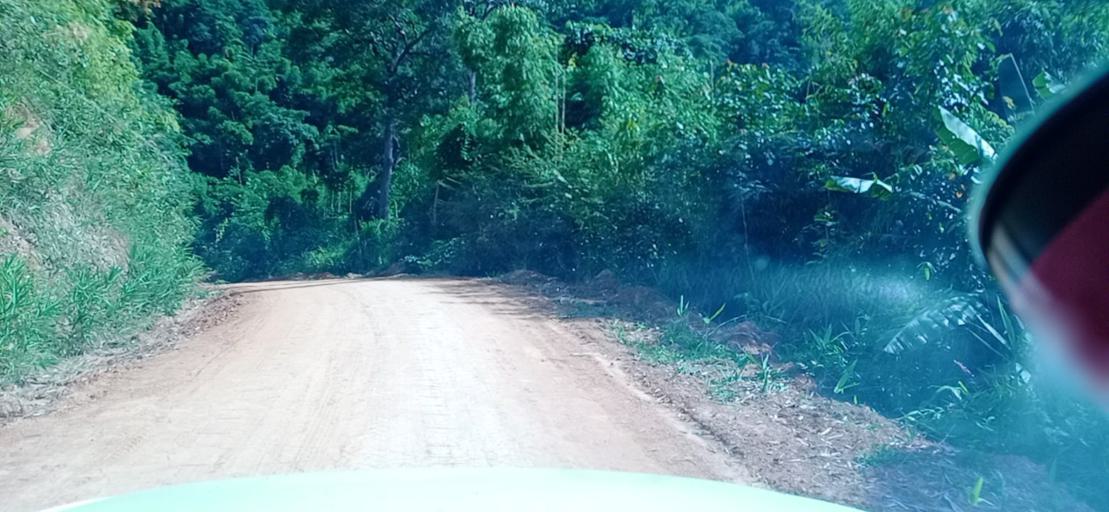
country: TH
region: Changwat Bueng Kan
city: Pak Khat
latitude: 18.6375
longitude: 103.2470
